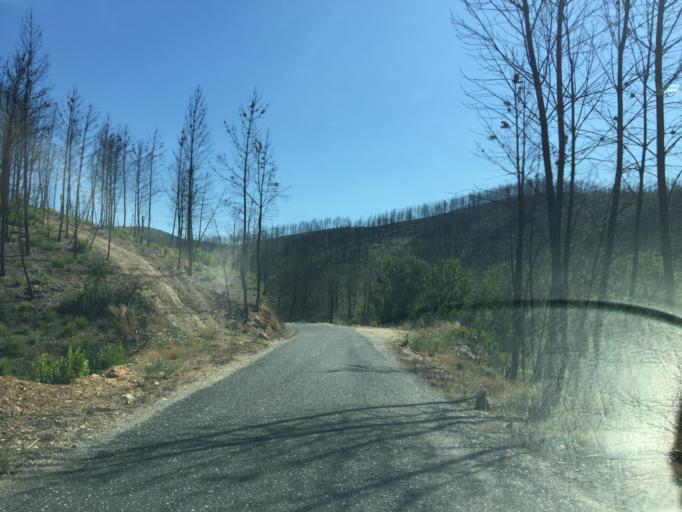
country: PT
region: Coimbra
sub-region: Pampilhosa da Serra
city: Pampilhosa da Serra
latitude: 40.0236
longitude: -7.8346
